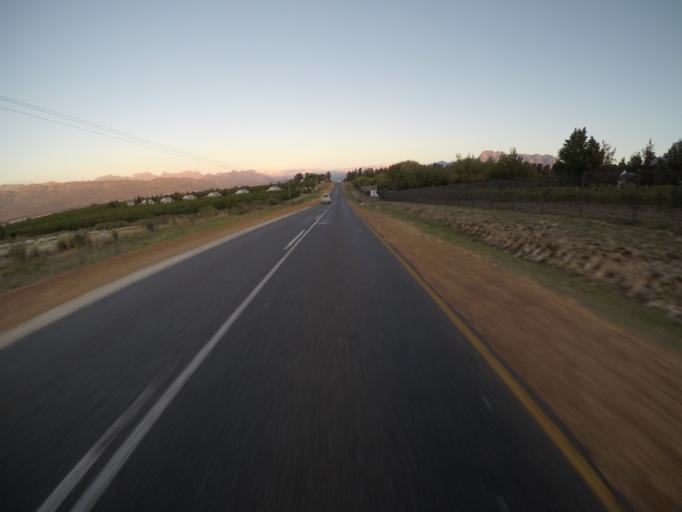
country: ZA
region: Western Cape
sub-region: Cape Winelands District Municipality
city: Paarl
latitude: -33.8265
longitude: 18.9374
